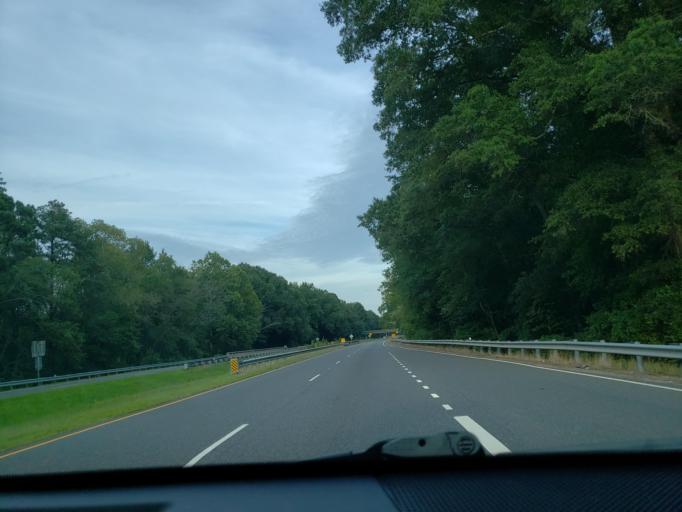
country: US
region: Virginia
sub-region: Brunswick County
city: Lawrenceville
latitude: 36.7482
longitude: -77.8520
